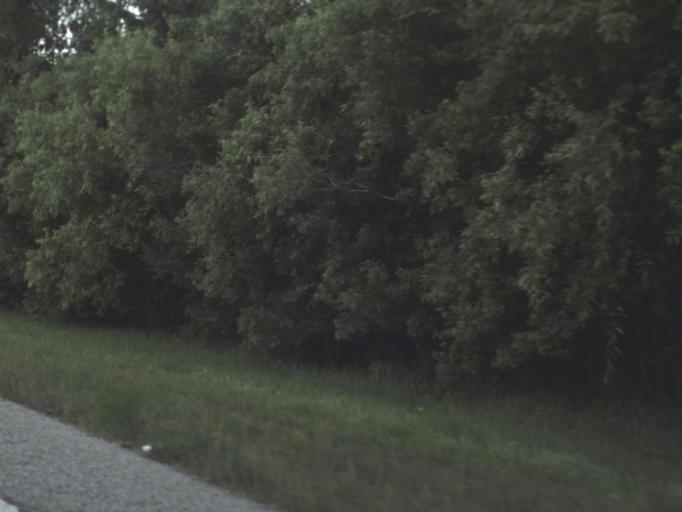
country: US
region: Florida
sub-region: Saint Johns County
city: Saint Augustine Shores
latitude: 29.7430
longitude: -81.3098
